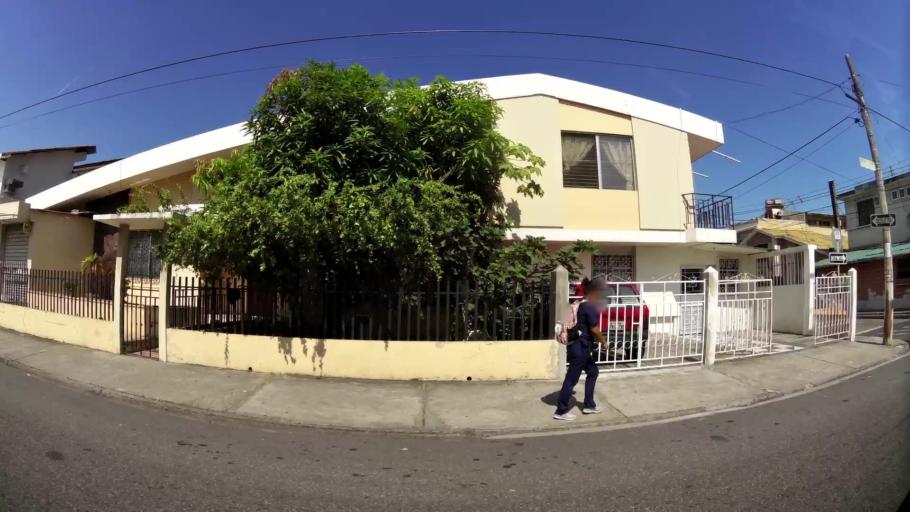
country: EC
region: Guayas
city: Guayaquil
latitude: -2.1650
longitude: -79.9150
